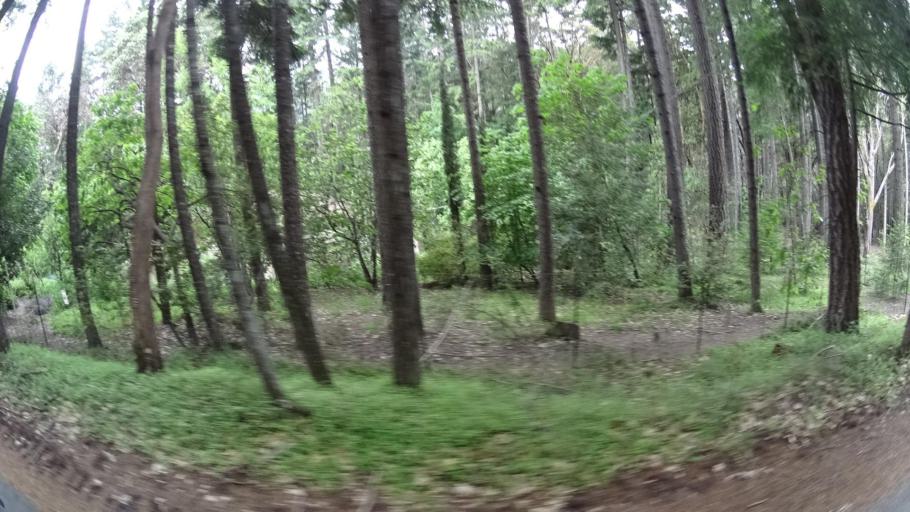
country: US
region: California
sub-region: Humboldt County
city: Willow Creek
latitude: 40.9300
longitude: -123.6161
